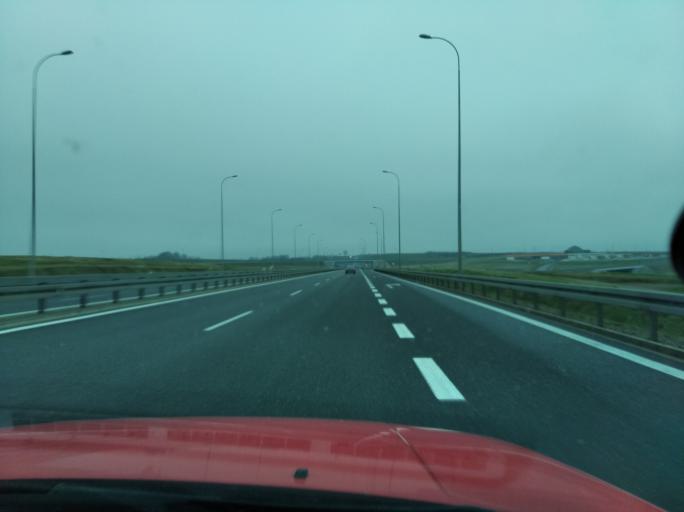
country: PL
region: Subcarpathian Voivodeship
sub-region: Powiat jaroslawski
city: Wierzbna
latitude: 50.0361
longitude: 22.5817
